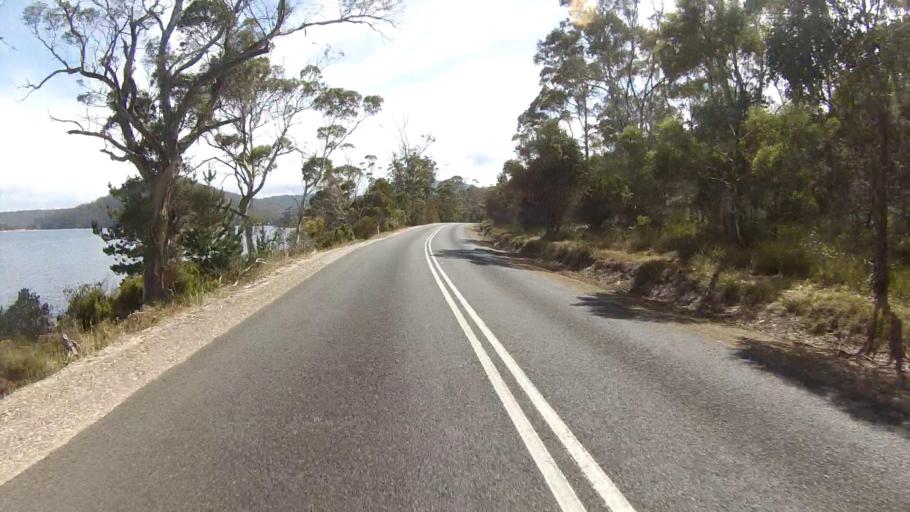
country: AU
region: Tasmania
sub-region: Huon Valley
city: Cygnet
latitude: -43.2642
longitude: 147.1429
